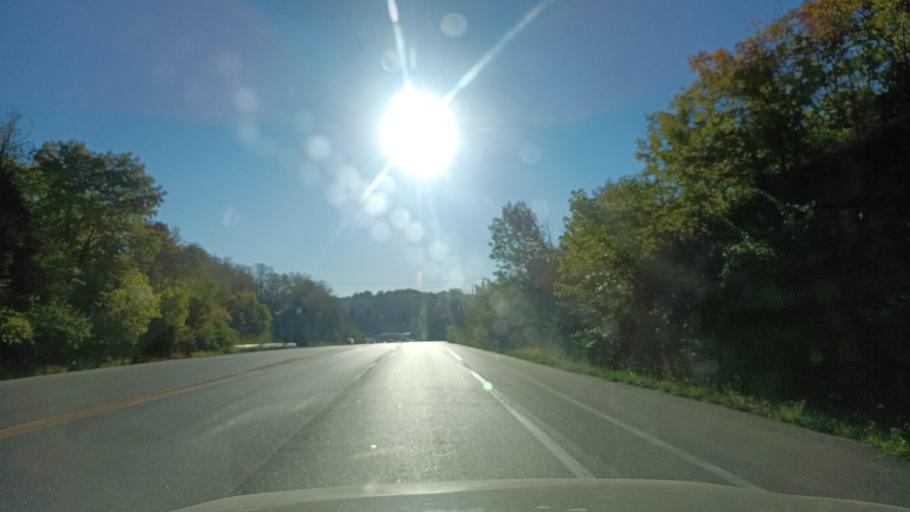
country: US
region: Missouri
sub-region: Boone County
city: Columbia
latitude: 38.9333
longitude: -92.3172
